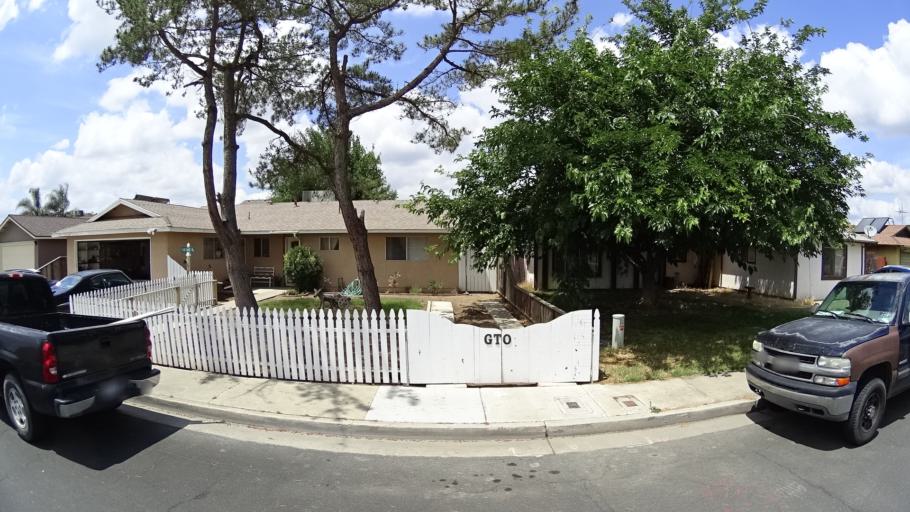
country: US
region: California
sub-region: Kings County
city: Armona
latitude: 36.3114
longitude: -119.6771
